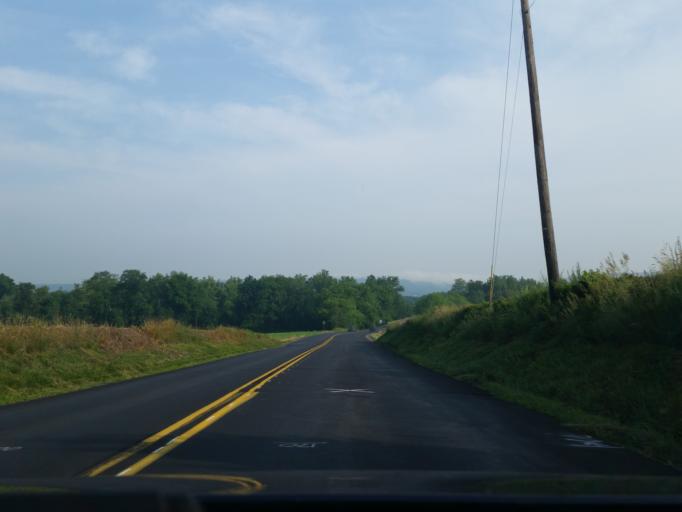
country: US
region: Pennsylvania
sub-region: Lebanon County
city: Annville
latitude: 40.3999
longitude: -76.5743
